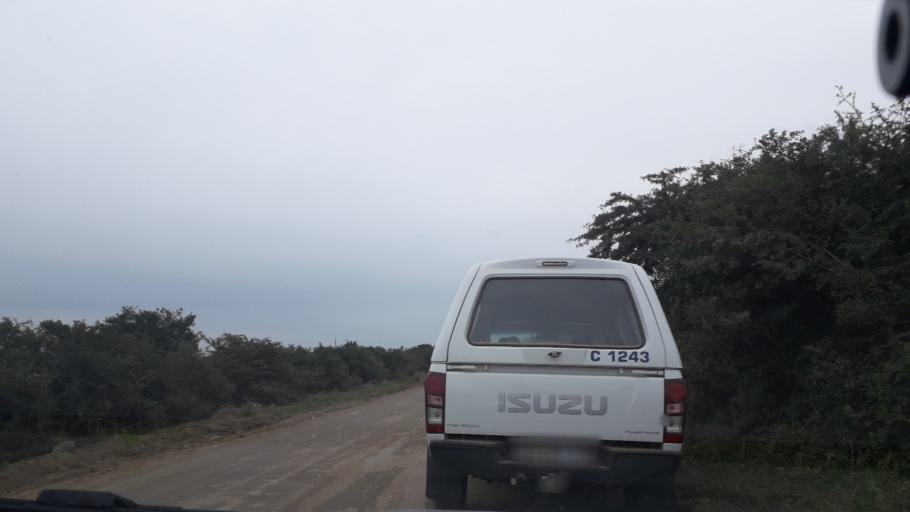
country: ZA
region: Eastern Cape
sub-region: Buffalo City Metropolitan Municipality
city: Bhisho
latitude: -32.7913
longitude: 27.3372
